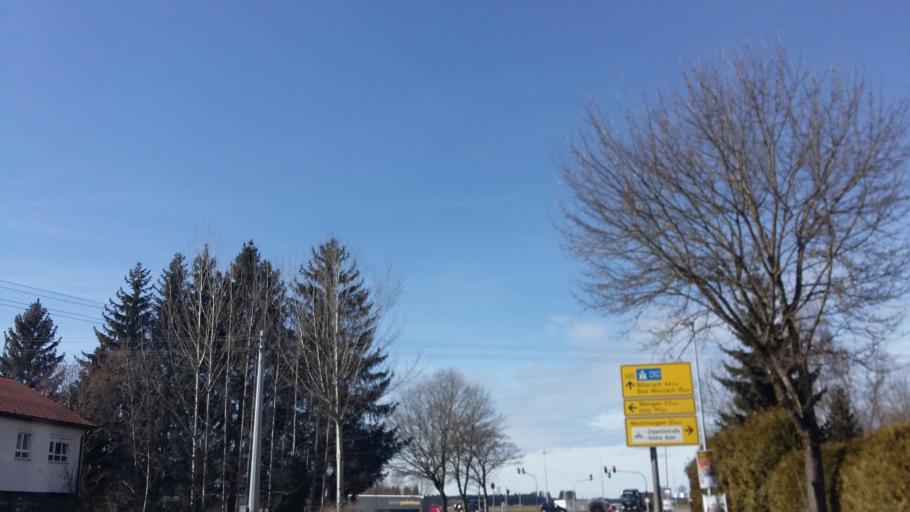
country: DE
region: Baden-Wuerttemberg
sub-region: Tuebingen Region
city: Leutkirch im Allgau
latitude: 47.8292
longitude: 10.0084
